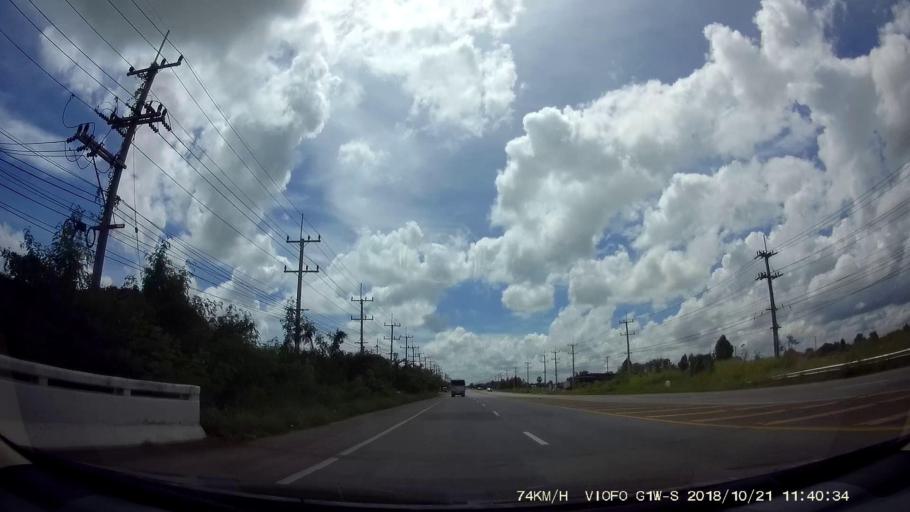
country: TH
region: Chaiyaphum
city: Chaiyaphum
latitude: 15.7113
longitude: 102.0155
